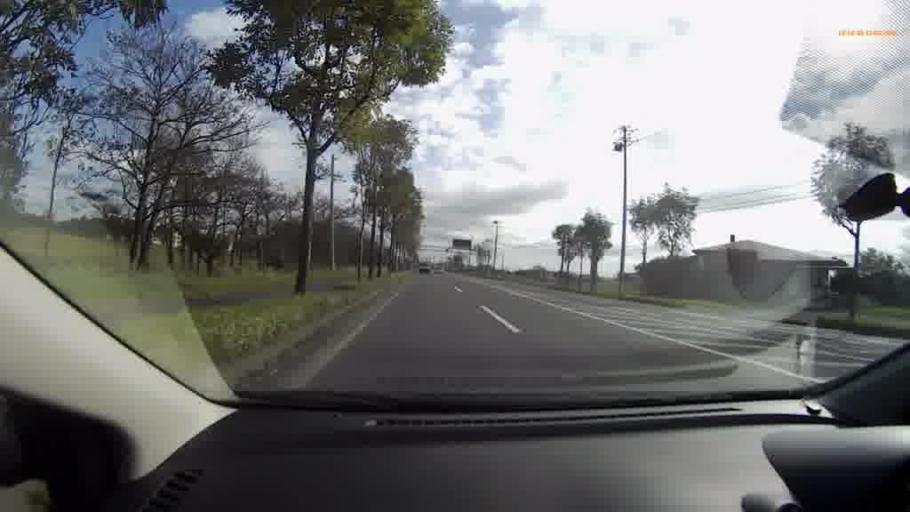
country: JP
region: Hokkaido
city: Kushiro
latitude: 43.0103
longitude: 144.2878
